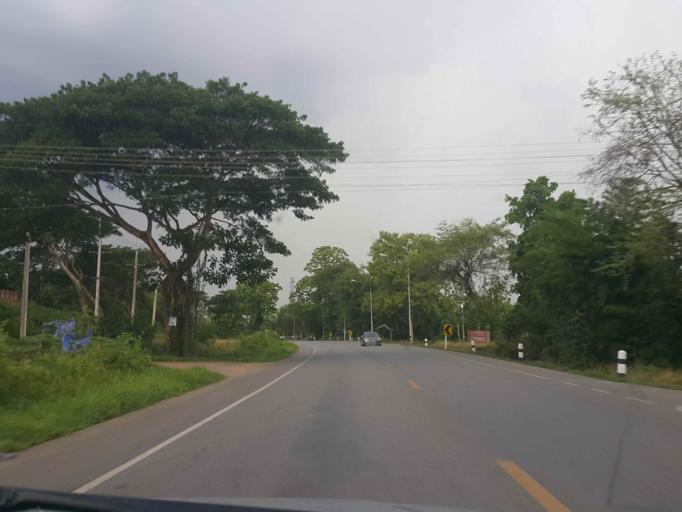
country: TH
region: Phrae
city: Den Chai
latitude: 17.9766
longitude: 100.0166
